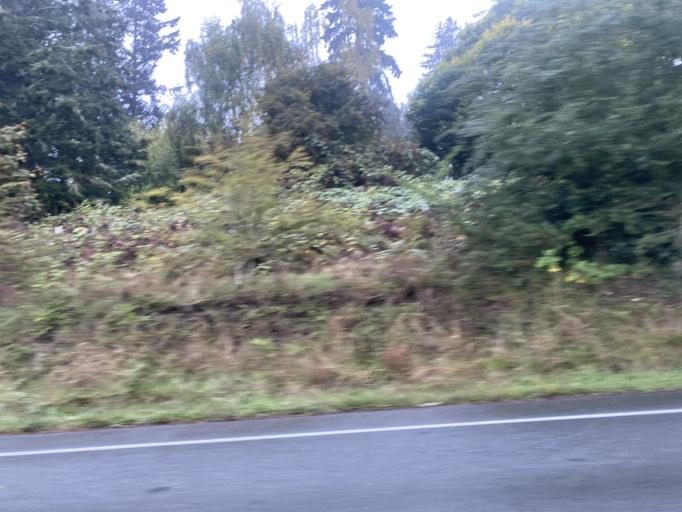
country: US
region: Washington
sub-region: Island County
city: Freeland
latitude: 48.0415
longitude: -122.5069
